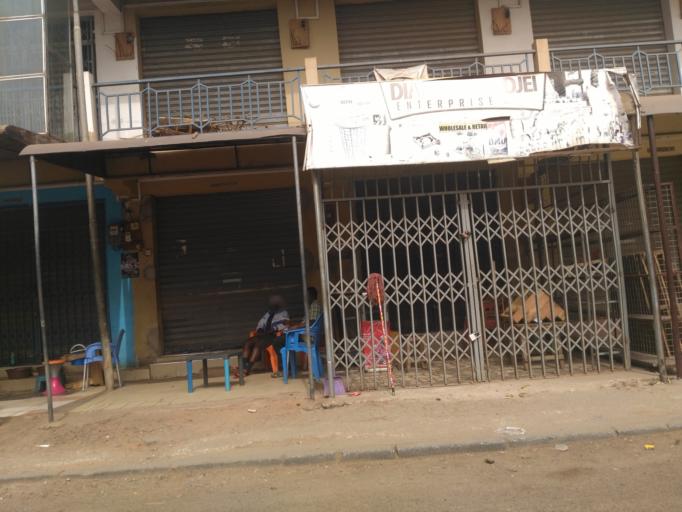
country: GH
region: Ashanti
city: Kumasi
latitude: 6.6849
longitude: -1.6140
